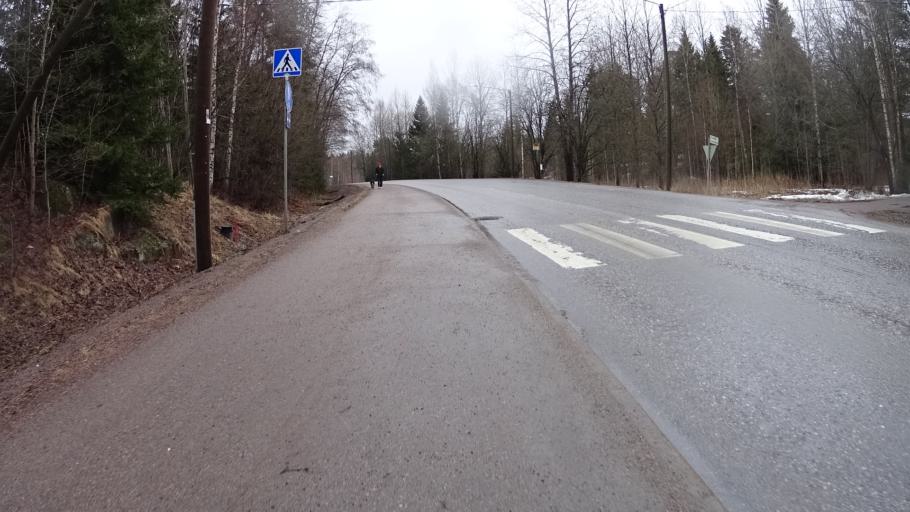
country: FI
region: Uusimaa
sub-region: Helsinki
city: Espoo
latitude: 60.1973
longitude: 24.5971
